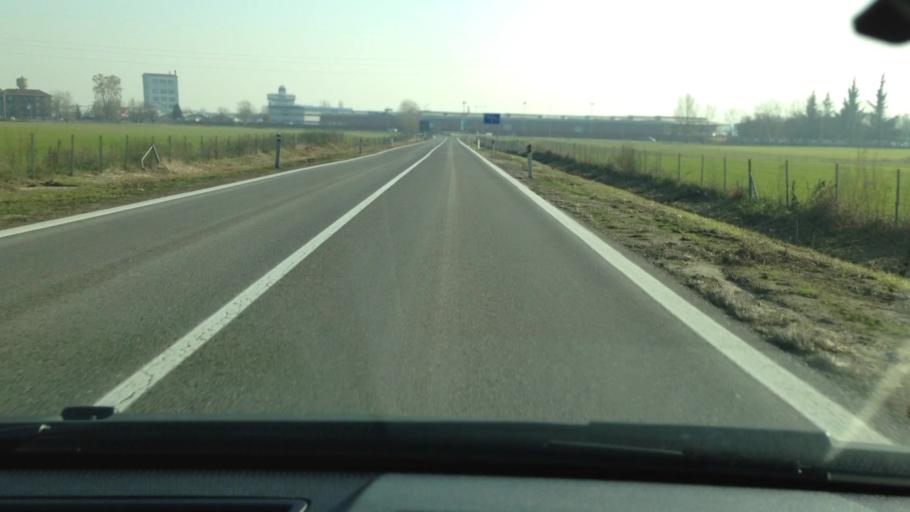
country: IT
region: Piedmont
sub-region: Provincia di Alessandria
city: Quattordio
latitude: 44.9019
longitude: 8.4175
